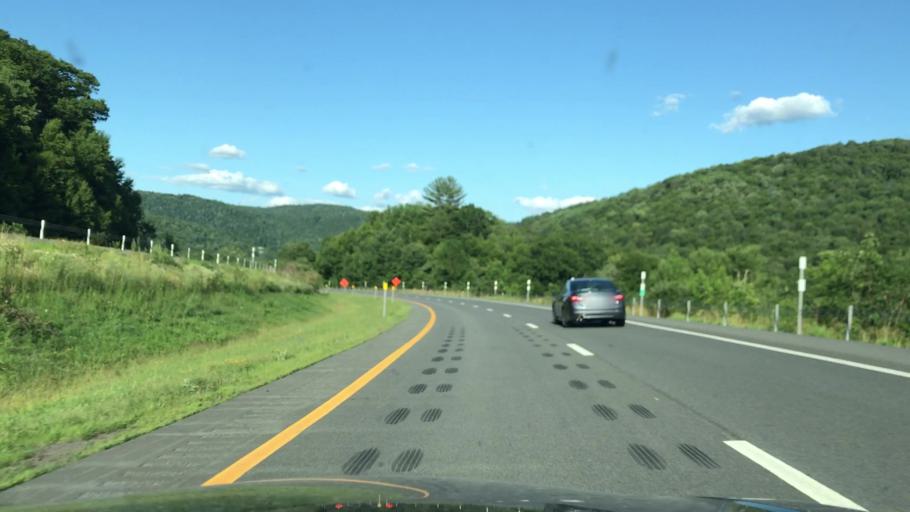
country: US
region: New York
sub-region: Delaware County
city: Walton
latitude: 41.9832
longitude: -75.0838
